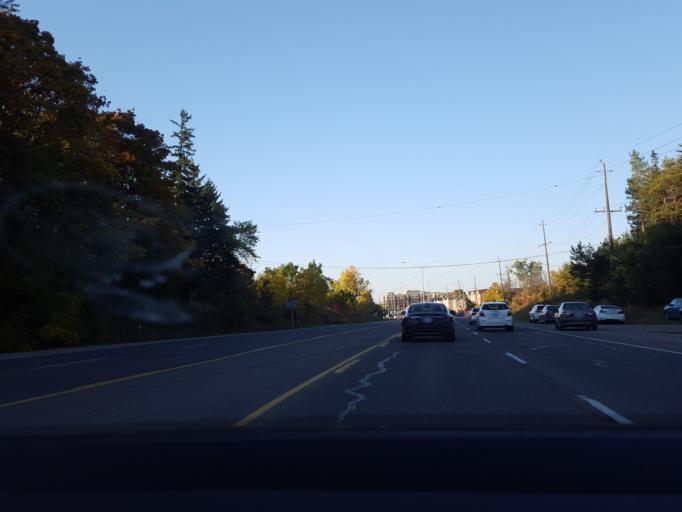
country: CA
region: Ontario
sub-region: York
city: Richmond Hill
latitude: 43.9365
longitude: -79.4536
